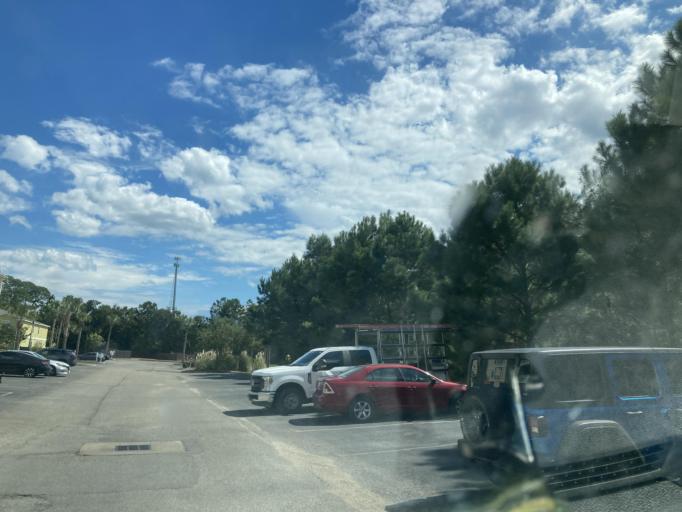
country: US
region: Mississippi
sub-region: Jackson County
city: Saint Martin
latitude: 30.4441
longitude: -88.8536
